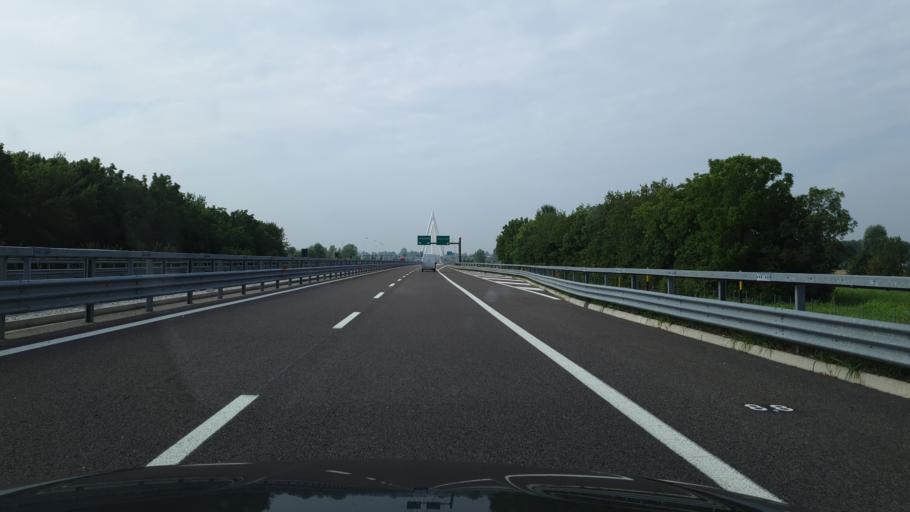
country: IT
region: Veneto
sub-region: Provincia di Padova
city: Piacenza d'Adige
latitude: 45.1350
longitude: 11.5308
